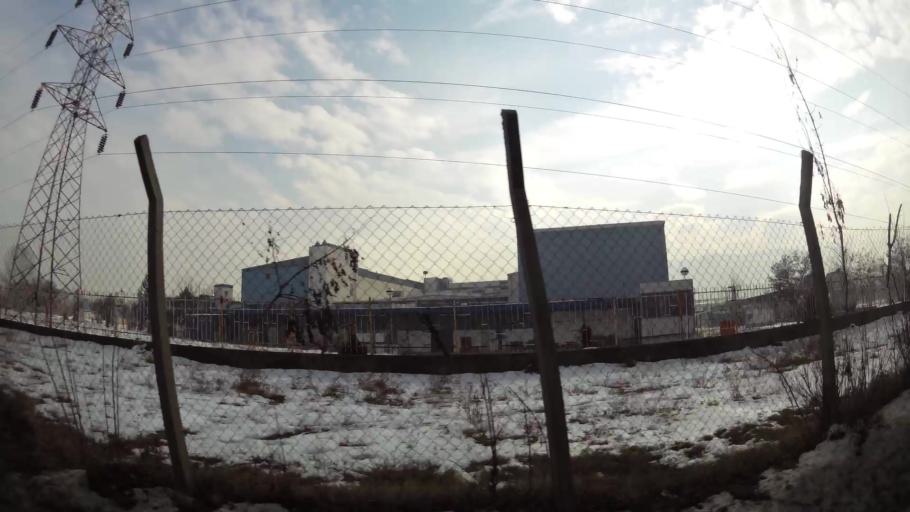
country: MK
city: Krushopek
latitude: 42.0140
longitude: 21.3631
